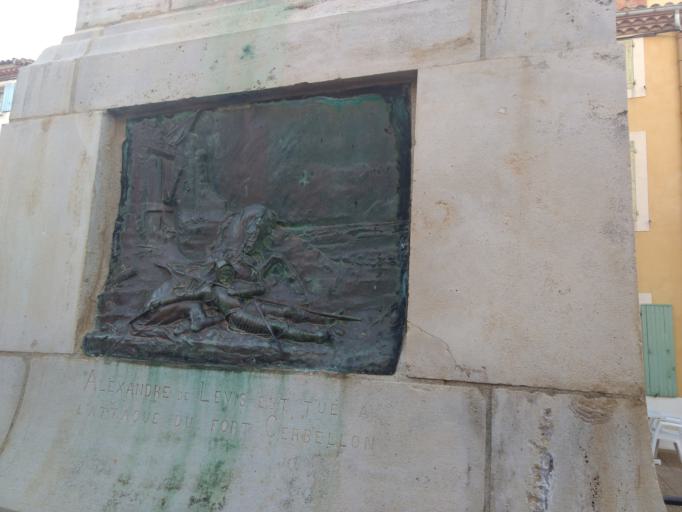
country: FR
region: Languedoc-Roussillon
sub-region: Departement de l'Aude
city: Leucate
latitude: 42.9098
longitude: 3.0271
